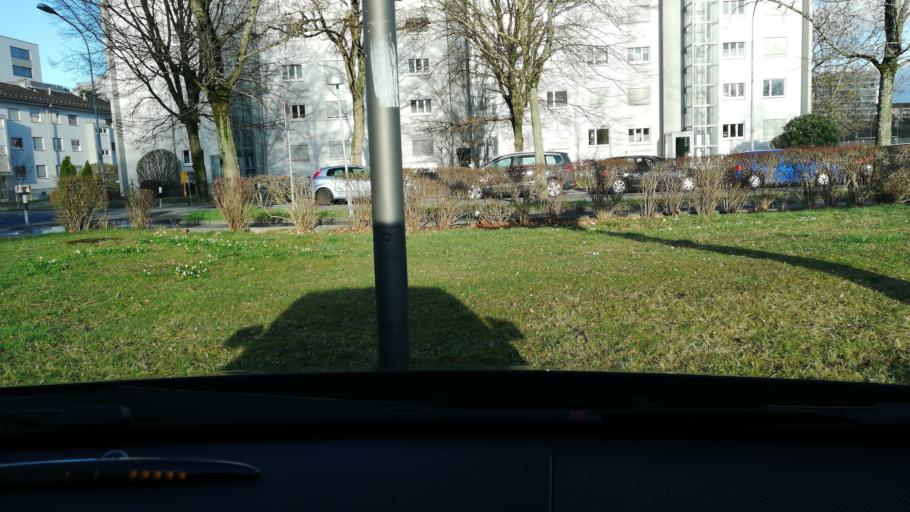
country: CH
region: Zurich
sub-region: Bezirk Zuerich
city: Zuerich (Kreis 12) / Hirzenbach
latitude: 47.4008
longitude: 8.5932
